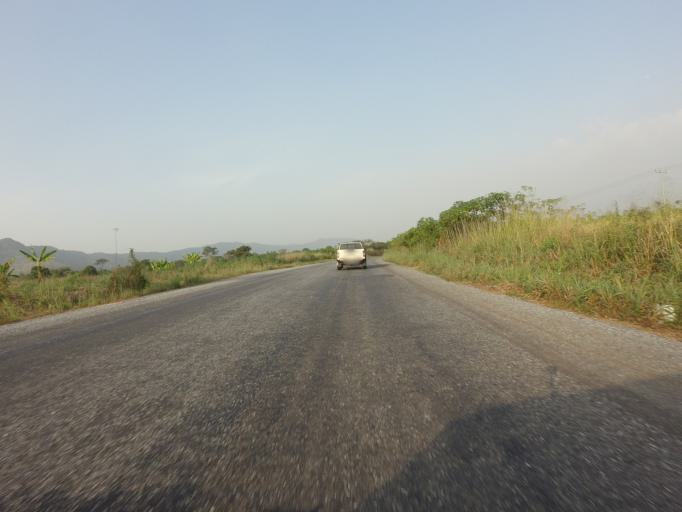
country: GH
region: Volta
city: Ho
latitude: 6.4564
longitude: 0.2152
